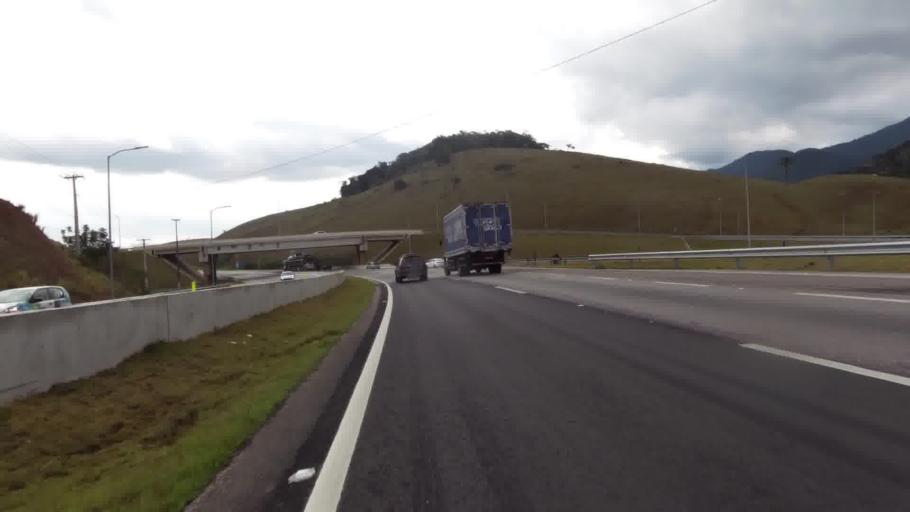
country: BR
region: Rio de Janeiro
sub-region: Casimiro De Abreu
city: Casimiro de Abreu
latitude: -22.4649
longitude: -42.0698
